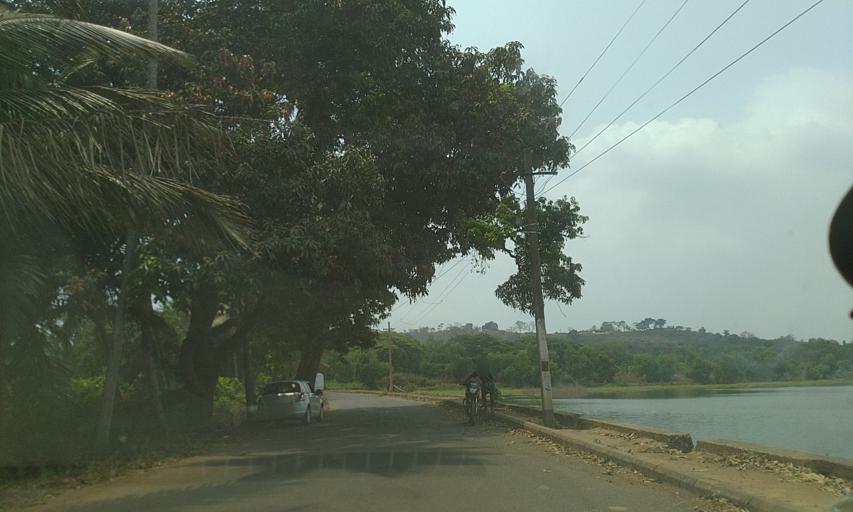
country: IN
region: Goa
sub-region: North Goa
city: Jua
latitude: 15.4864
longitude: 73.9270
